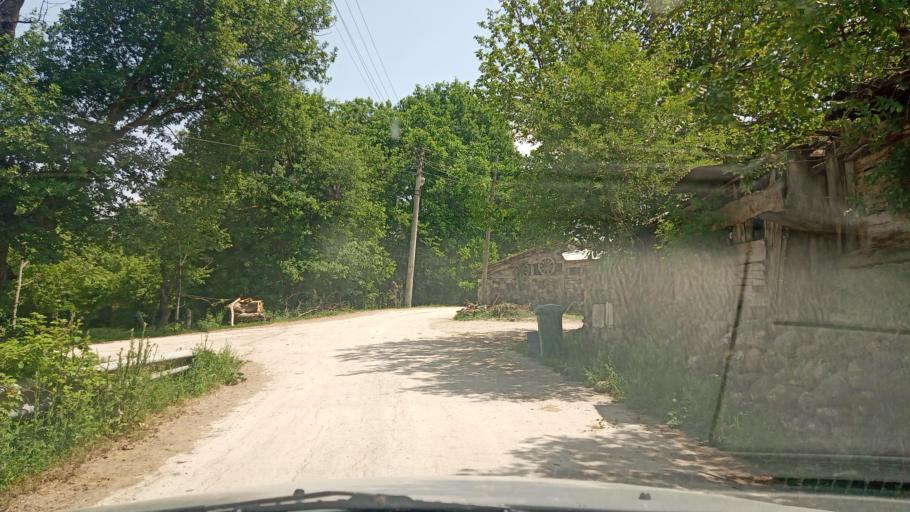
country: TR
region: Bolu
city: Seben
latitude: 40.4143
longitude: 31.5791
